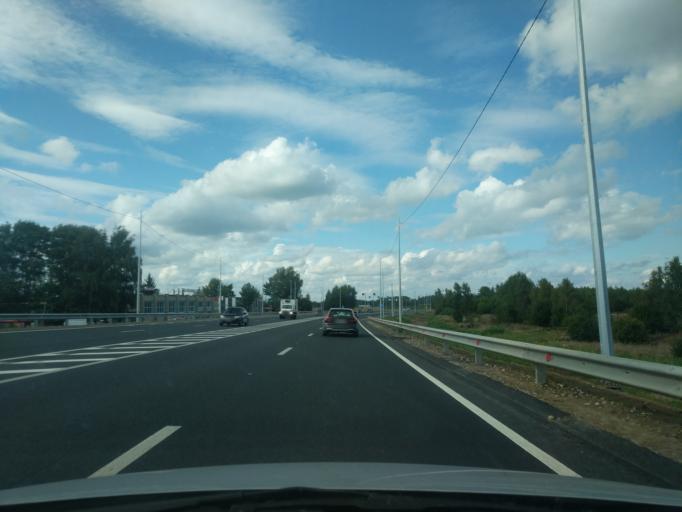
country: RU
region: Kostroma
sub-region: Kostromskoy Rayon
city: Kostroma
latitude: 57.7314
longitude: 40.8706
